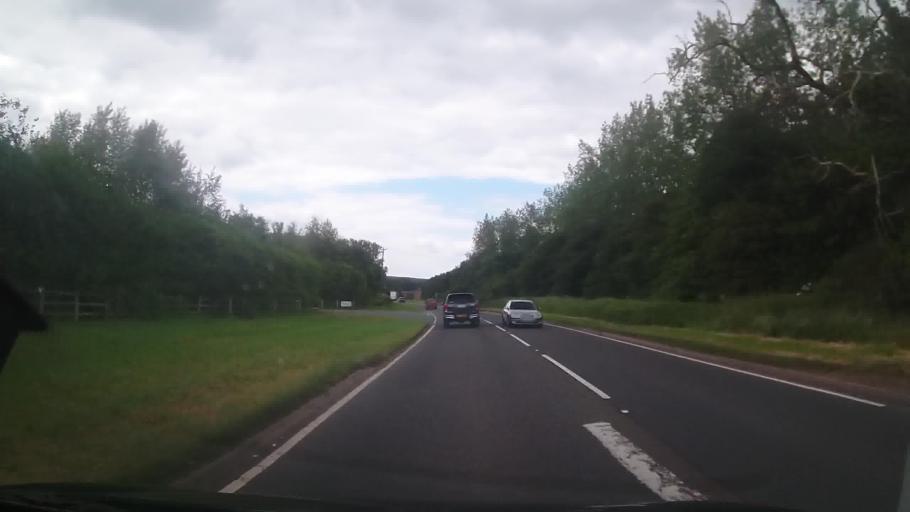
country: GB
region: England
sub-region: Herefordshire
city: Wellington
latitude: 52.1091
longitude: -2.7300
